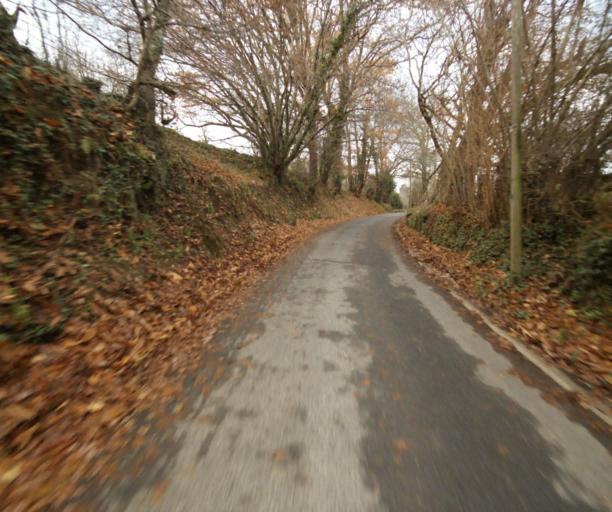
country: FR
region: Limousin
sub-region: Departement de la Correze
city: Chameyrat
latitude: 45.2404
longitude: 1.7246
